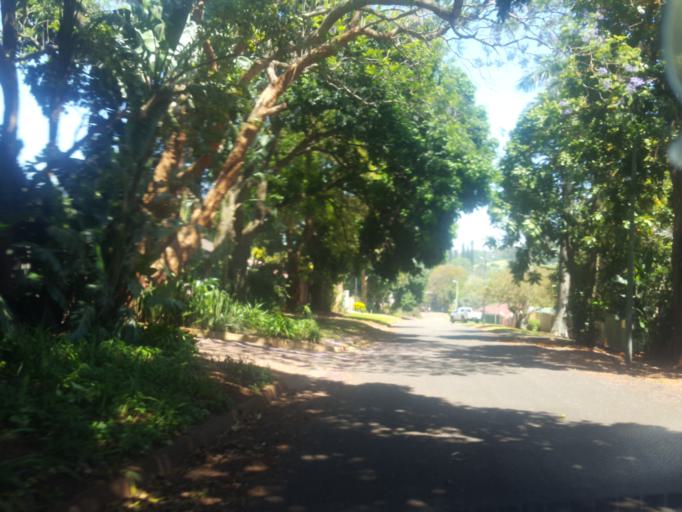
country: ZA
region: KwaZulu-Natal
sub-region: uThungulu District Municipality
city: Empangeni
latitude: -28.7485
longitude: 31.9048
